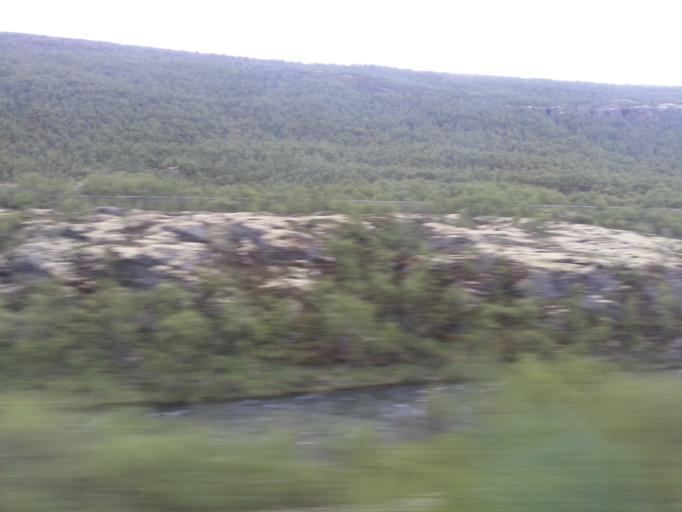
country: NO
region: Sor-Trondelag
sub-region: Oppdal
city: Oppdal
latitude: 62.3112
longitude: 9.6096
